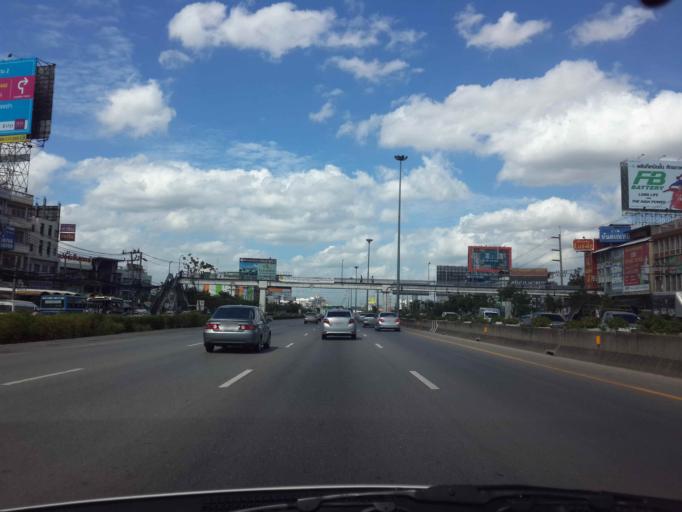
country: TH
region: Bangkok
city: Bang Khun Thian
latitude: 13.6490
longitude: 100.4194
